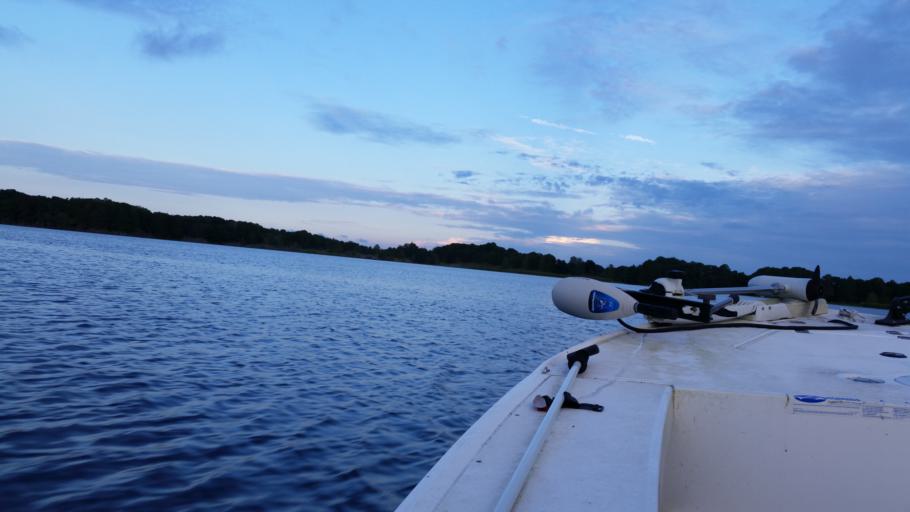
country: US
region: Florida
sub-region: Citrus County
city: Inverness
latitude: 28.8315
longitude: -82.3017
